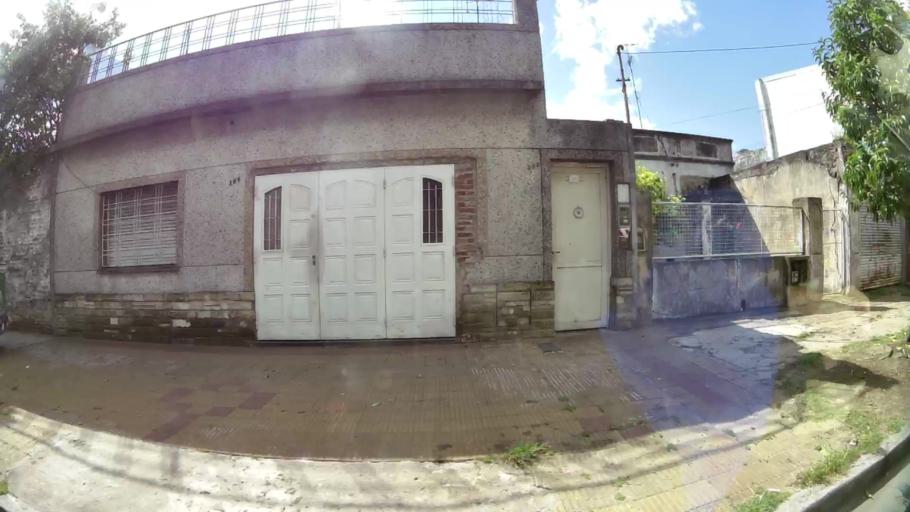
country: AR
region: Buenos Aires
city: San Justo
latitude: -34.6494
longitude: -58.5483
